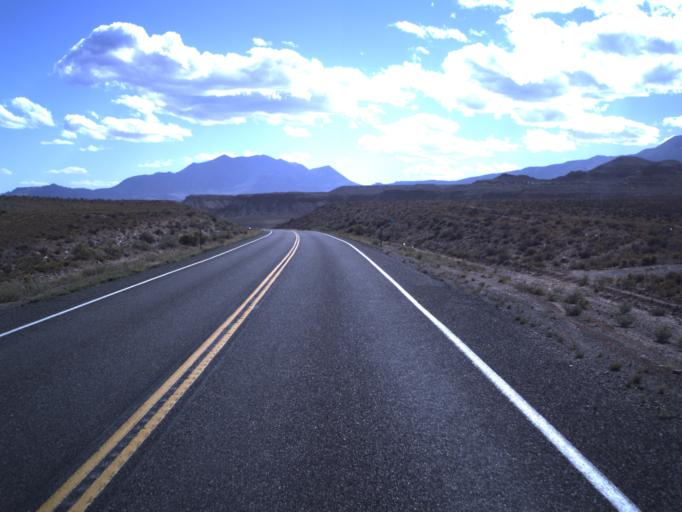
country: US
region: Utah
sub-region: Wayne County
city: Loa
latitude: 38.1172
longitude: -110.6232
